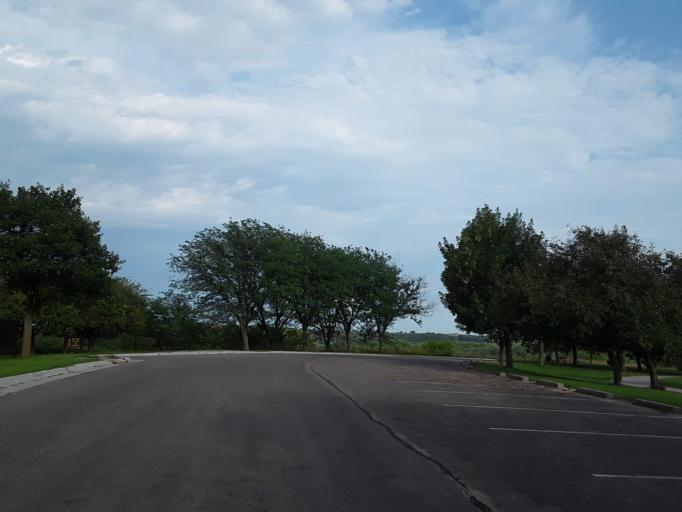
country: US
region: Nebraska
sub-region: Saunders County
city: Ashland
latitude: 41.0254
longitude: -96.3090
